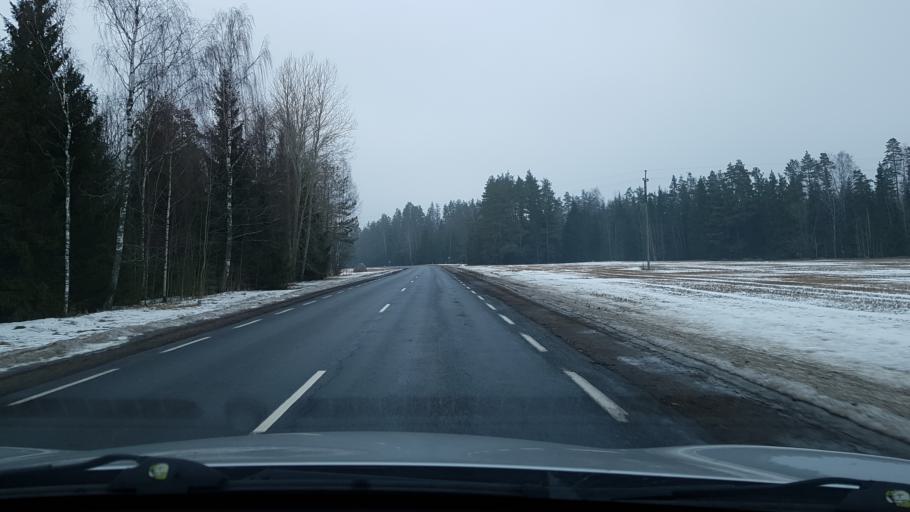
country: EE
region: Valgamaa
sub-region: Torva linn
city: Torva
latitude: 58.1669
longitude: 25.9633
